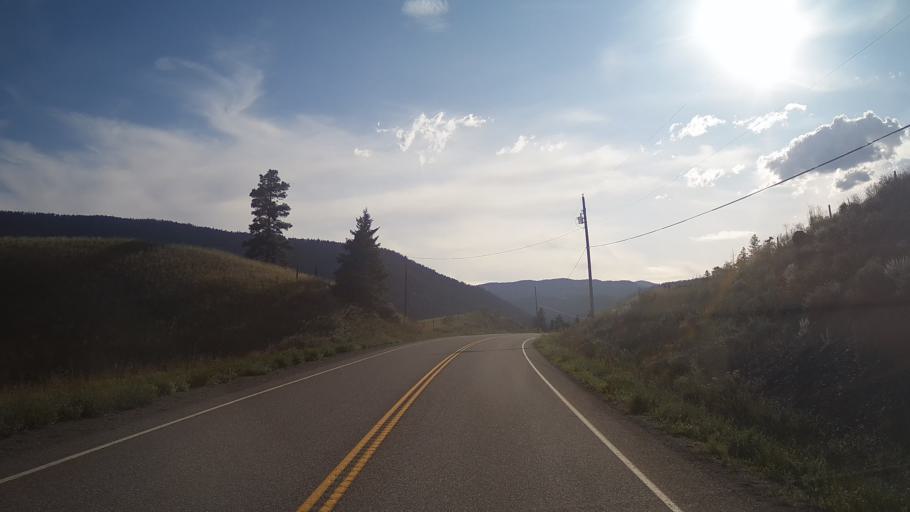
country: CA
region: British Columbia
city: Cache Creek
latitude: 50.8871
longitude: -121.4561
